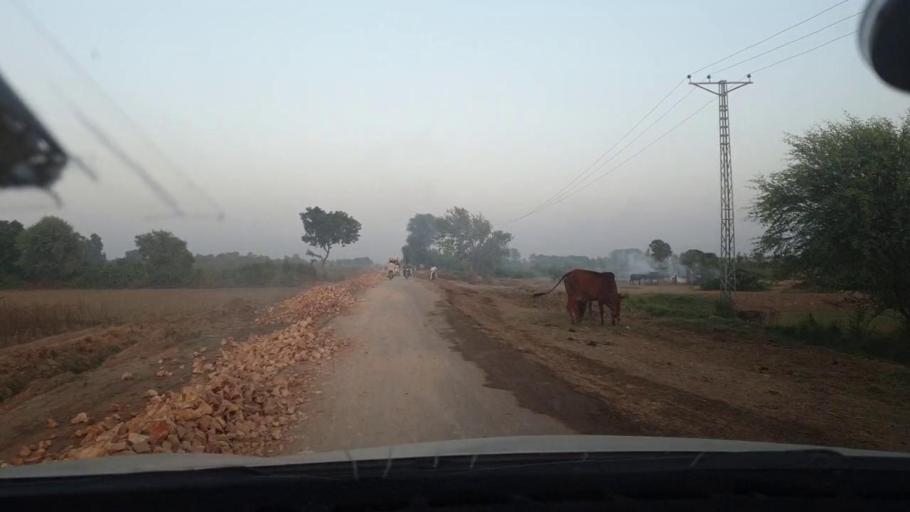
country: PK
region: Sindh
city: Bhit Shah
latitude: 25.7527
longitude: 68.5101
